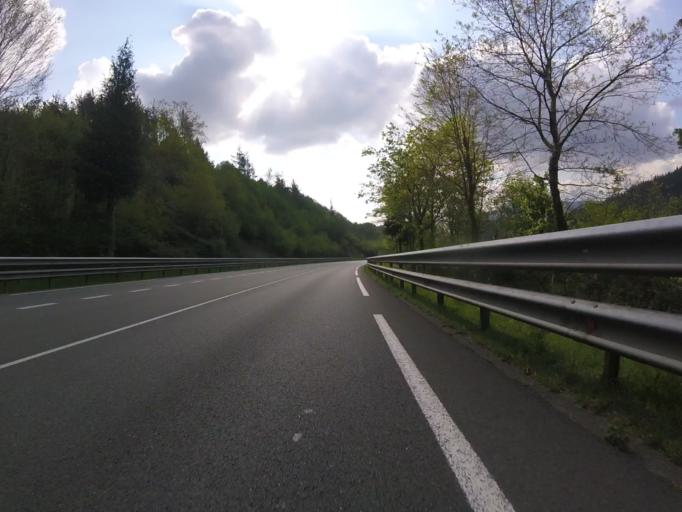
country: ES
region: Basque Country
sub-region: Provincia de Guipuzcoa
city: Azkoitia
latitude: 43.1978
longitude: -2.3397
